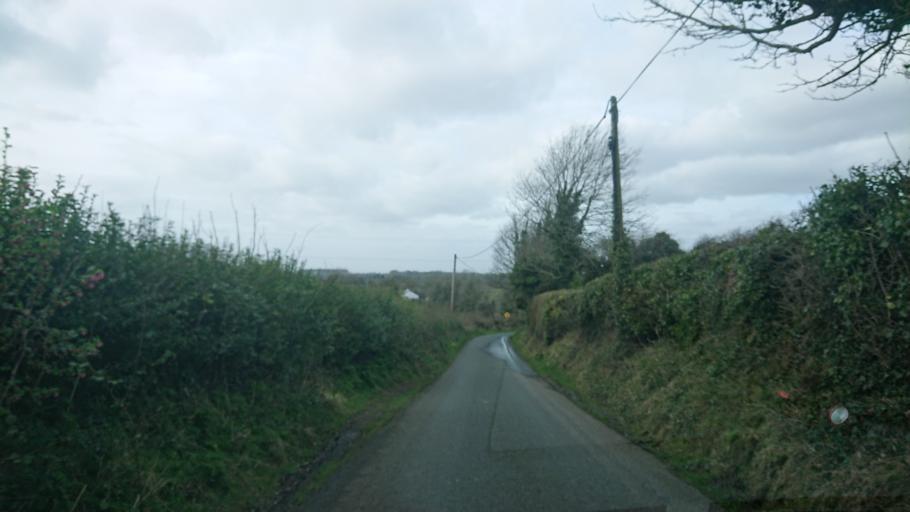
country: IE
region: Leinster
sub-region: Kildare
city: Eadestown
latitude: 53.1654
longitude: -6.6106
